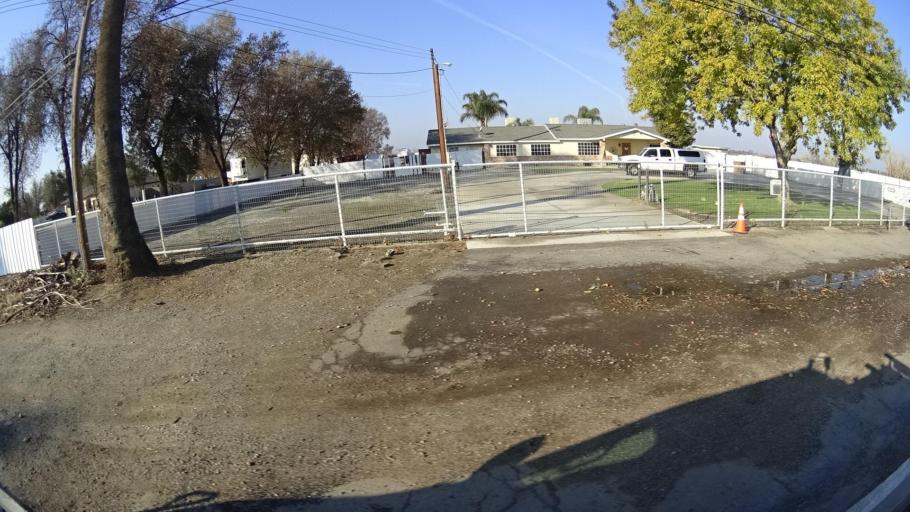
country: US
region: California
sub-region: Kern County
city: Greenfield
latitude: 35.2196
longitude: -119.0032
